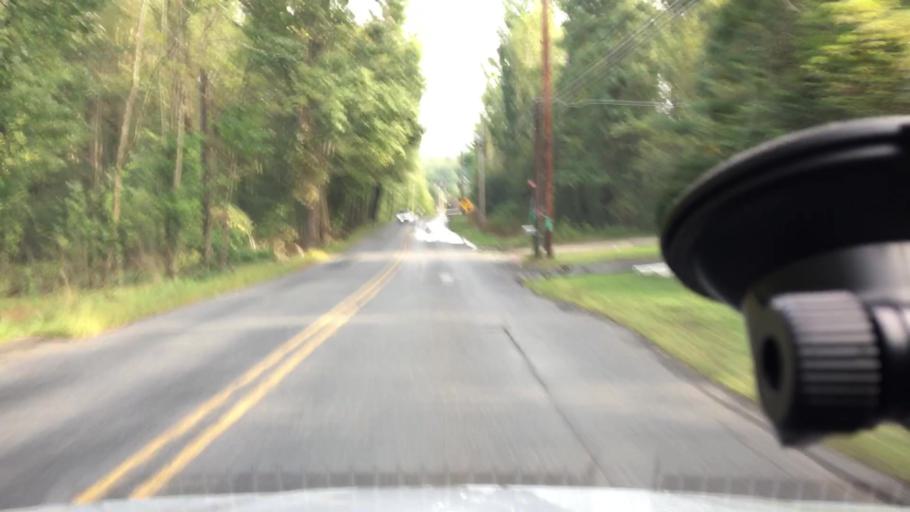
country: US
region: Pennsylvania
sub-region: Monroe County
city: Mount Pocono
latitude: 41.1249
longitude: -75.3113
